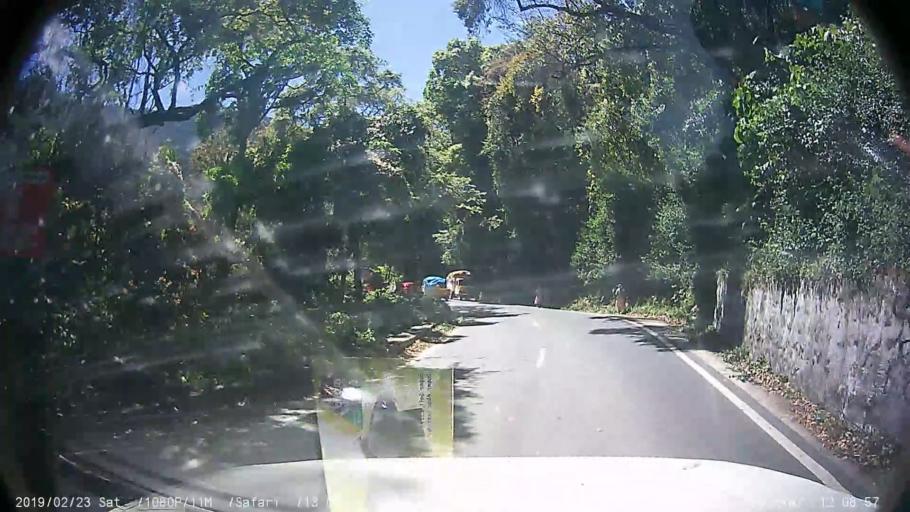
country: IN
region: Tamil Nadu
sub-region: Nilgiri
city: Wellington
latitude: 11.3316
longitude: 76.8085
